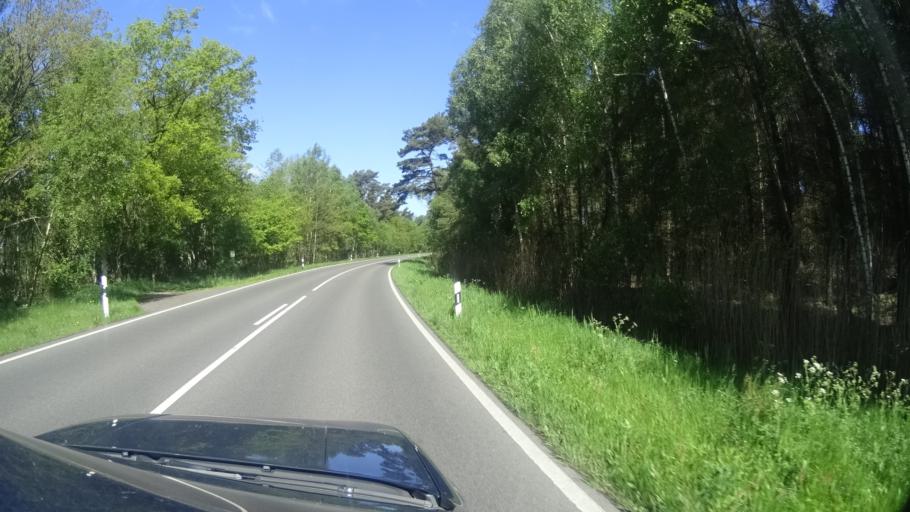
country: DE
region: Mecklenburg-Vorpommern
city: Zingst
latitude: 54.4208
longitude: 12.6528
